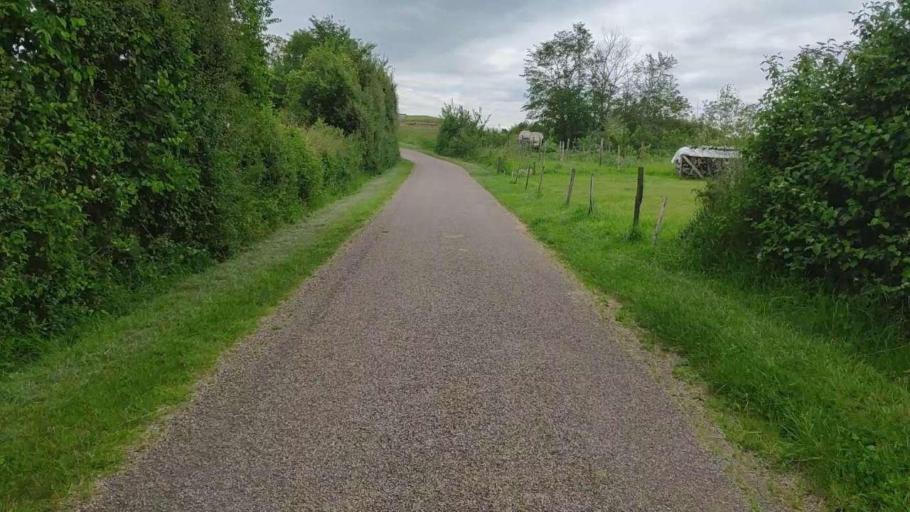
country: FR
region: Franche-Comte
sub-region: Departement du Jura
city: Lons-le-Saunier
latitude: 46.7553
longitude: 5.5652
